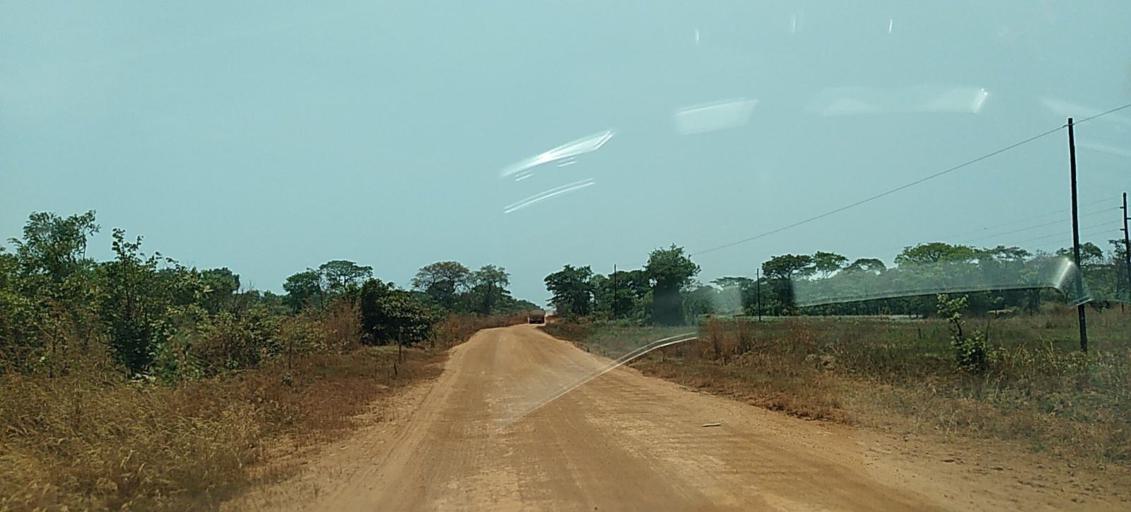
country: CD
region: Katanga
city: Kipushi
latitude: -11.9271
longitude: 26.9976
